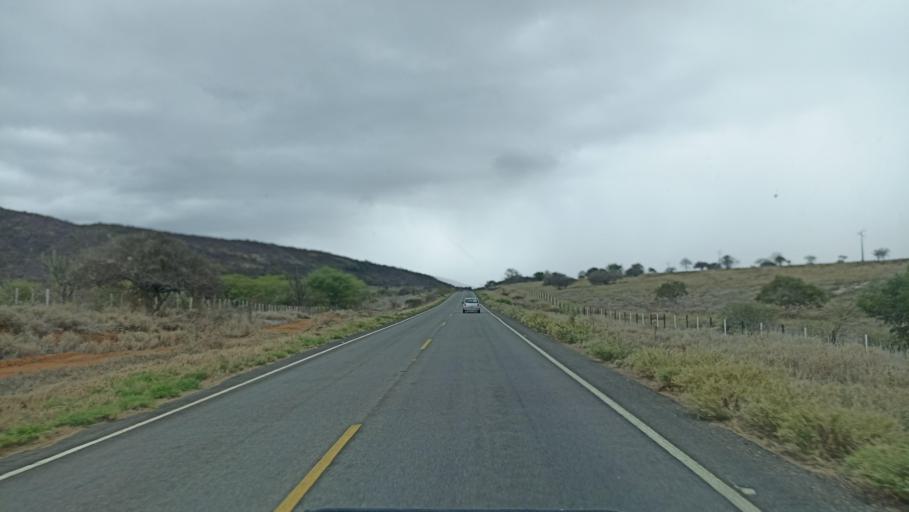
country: BR
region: Bahia
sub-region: Iacu
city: Iacu
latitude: -12.8098
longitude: -40.1158
